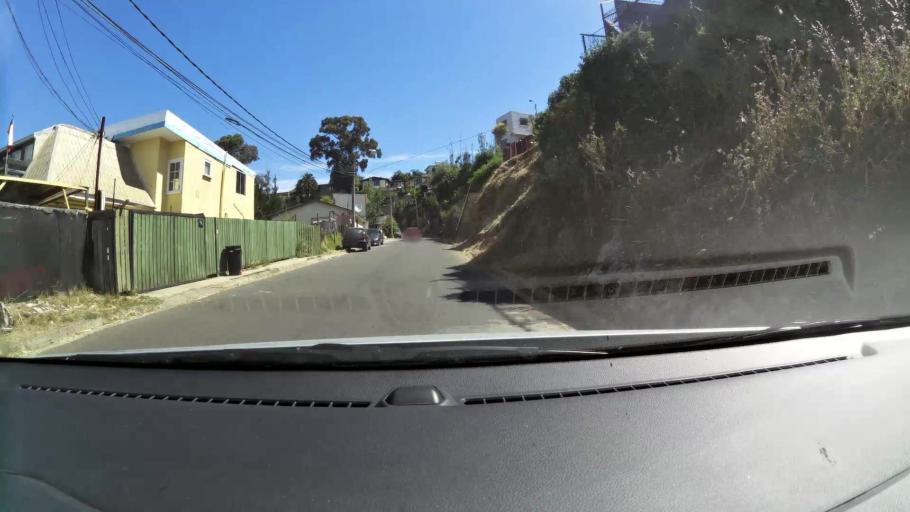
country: CL
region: Valparaiso
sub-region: Provincia de Valparaiso
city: Vina del Mar
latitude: -33.0391
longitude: -71.5770
